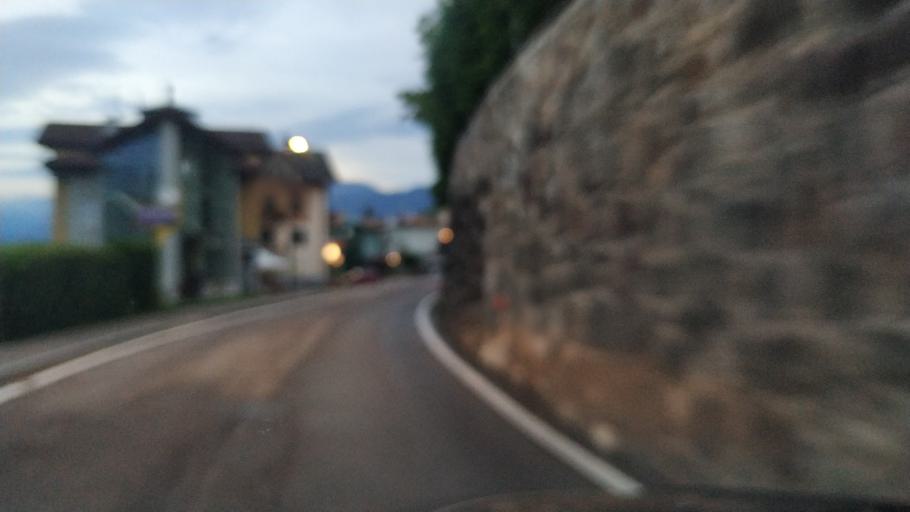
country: IT
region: Trentino-Alto Adige
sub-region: Provincia di Trento
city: Cloz
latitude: 46.4198
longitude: 11.0877
